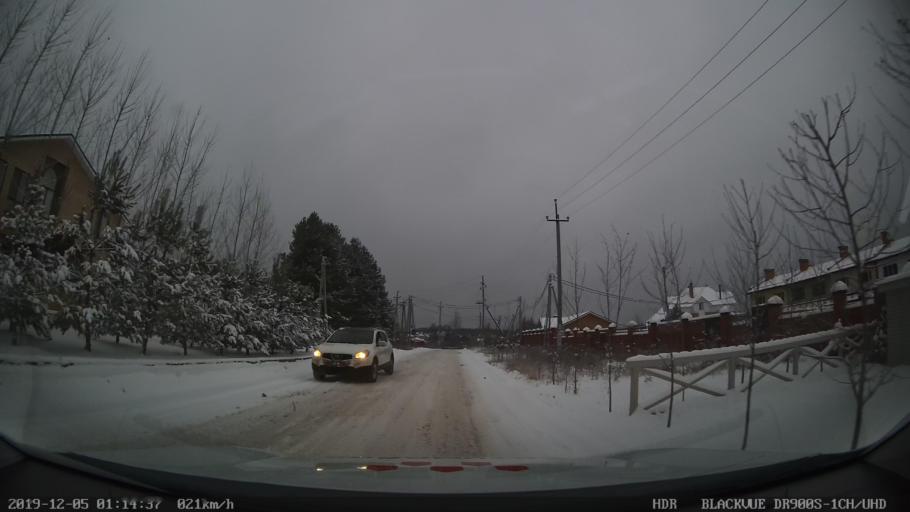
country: RU
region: Tatarstan
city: Stolbishchi
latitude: 55.6430
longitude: 49.1146
